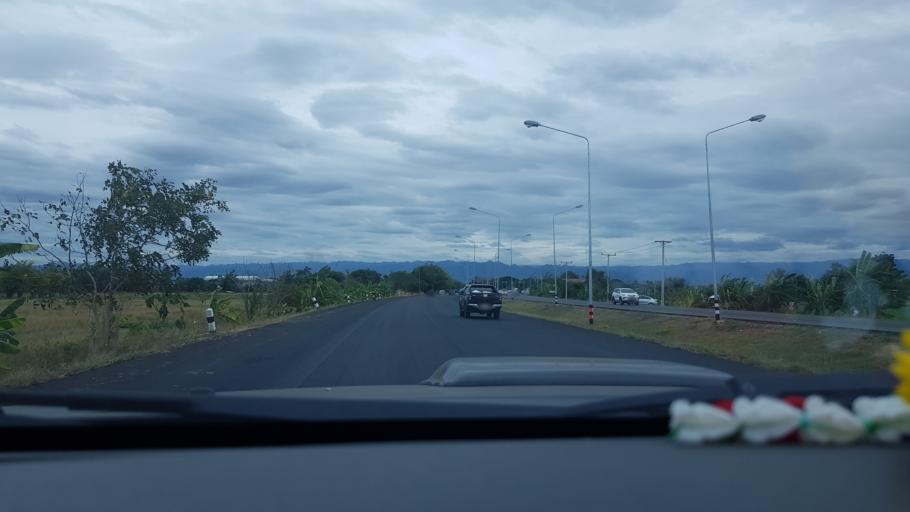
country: TH
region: Phetchabun
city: Phetchabun
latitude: 16.4970
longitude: 101.1510
